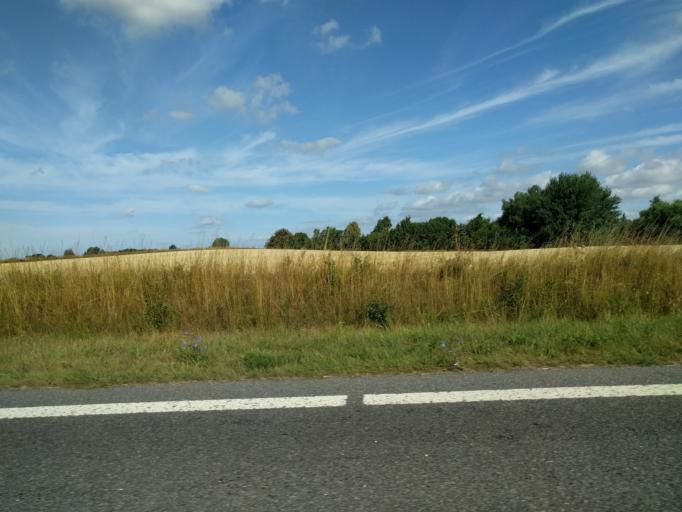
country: DK
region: Zealand
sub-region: Guldborgsund Kommune
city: Stubbekobing
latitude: 54.9150
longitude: 12.1441
